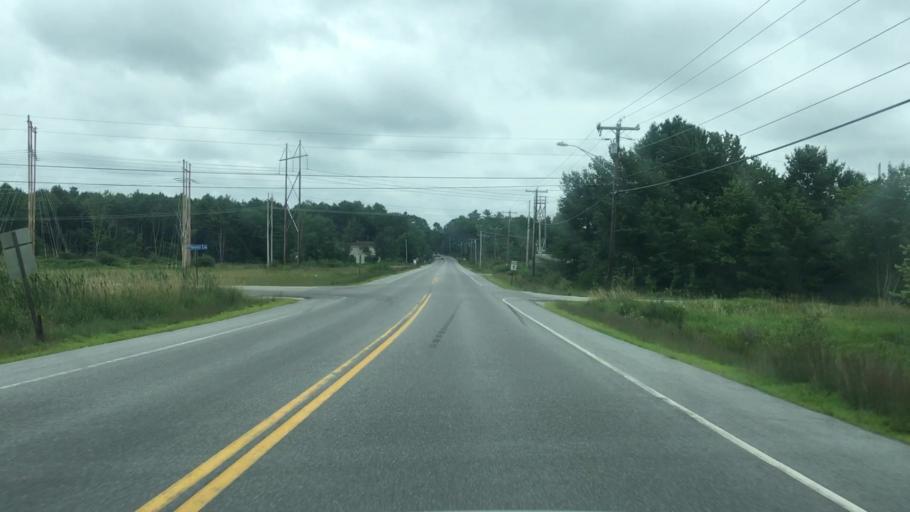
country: US
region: Maine
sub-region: York County
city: Biddeford
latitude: 43.5308
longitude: -70.5044
